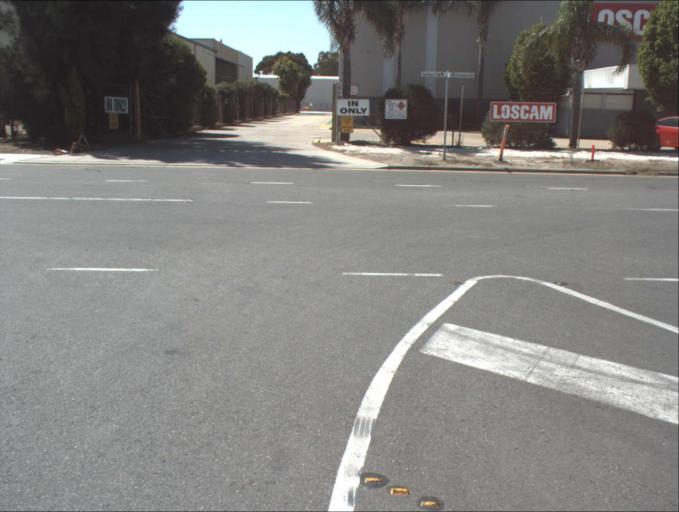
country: AU
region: South Australia
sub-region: Charles Sturt
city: Woodville North
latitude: -34.8409
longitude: 138.5594
